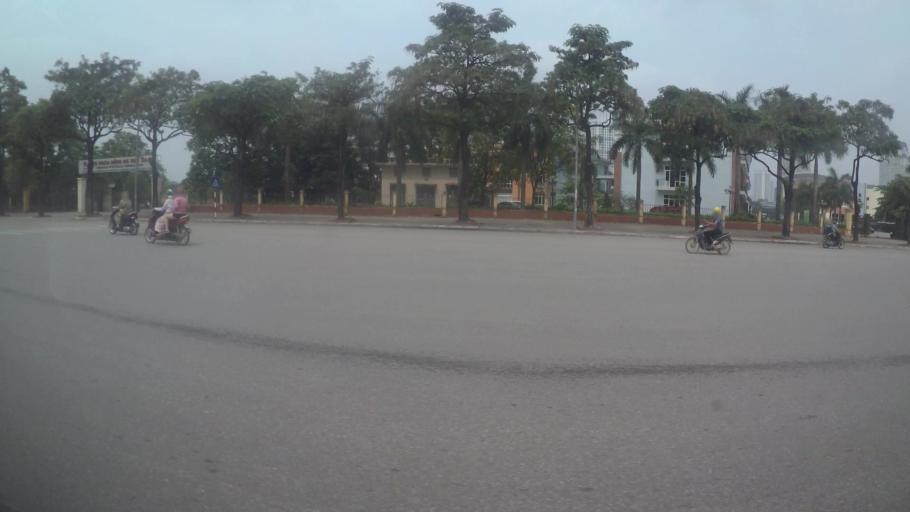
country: VN
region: Ha Noi
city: Cau Dien
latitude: 21.0159
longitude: 105.7683
